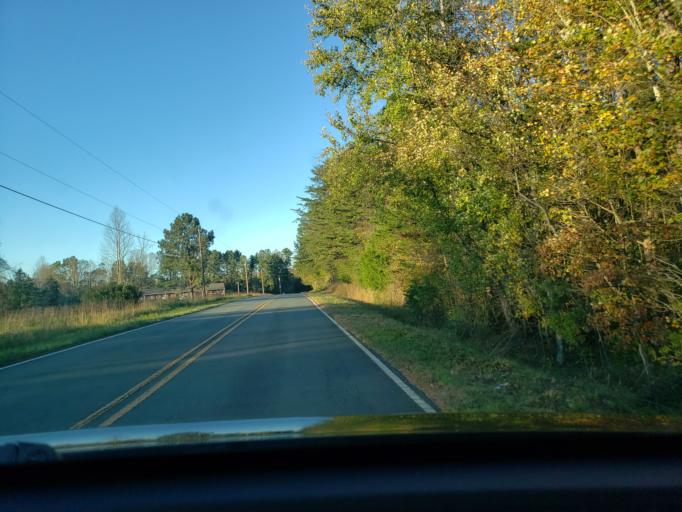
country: US
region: North Carolina
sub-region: Forsyth County
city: Walkertown
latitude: 36.2339
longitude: -80.2005
